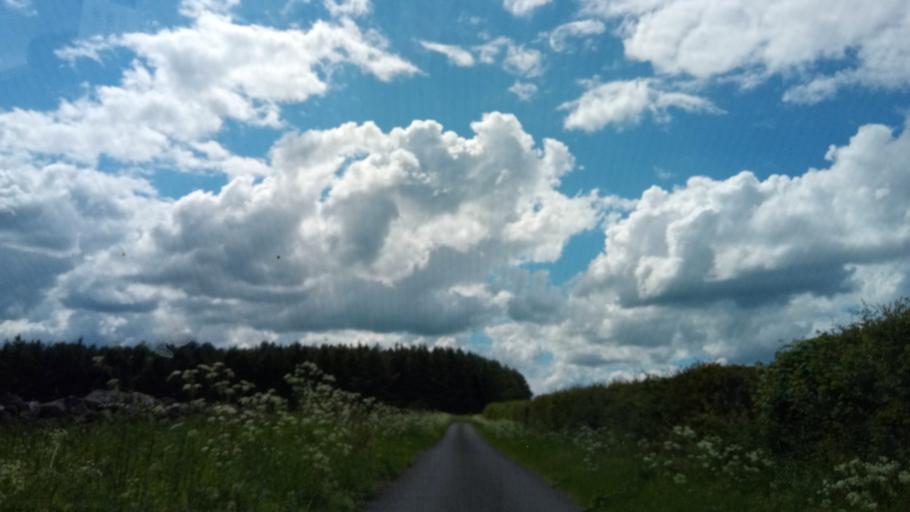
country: GB
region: Scotland
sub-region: The Scottish Borders
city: Coldstream
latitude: 55.6034
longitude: -2.2671
